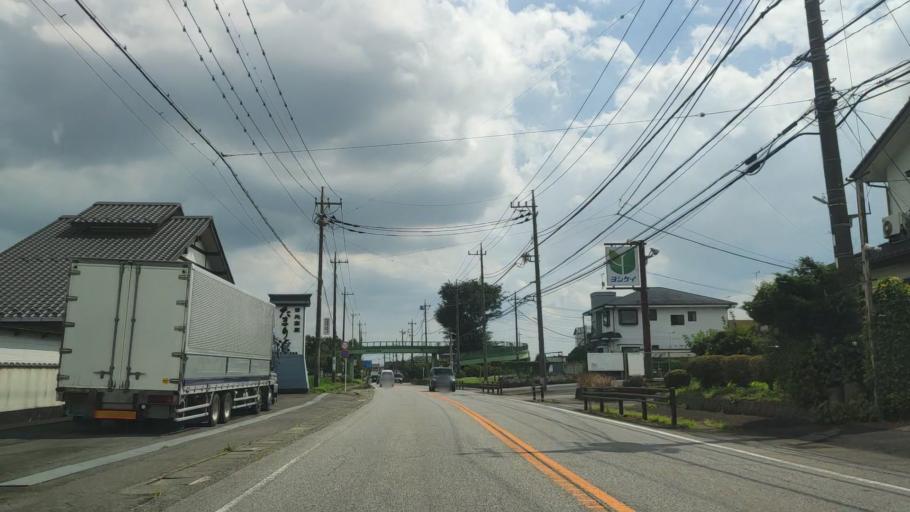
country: JP
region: Tochigi
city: Utsunomiya-shi
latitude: 36.6556
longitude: 139.8410
